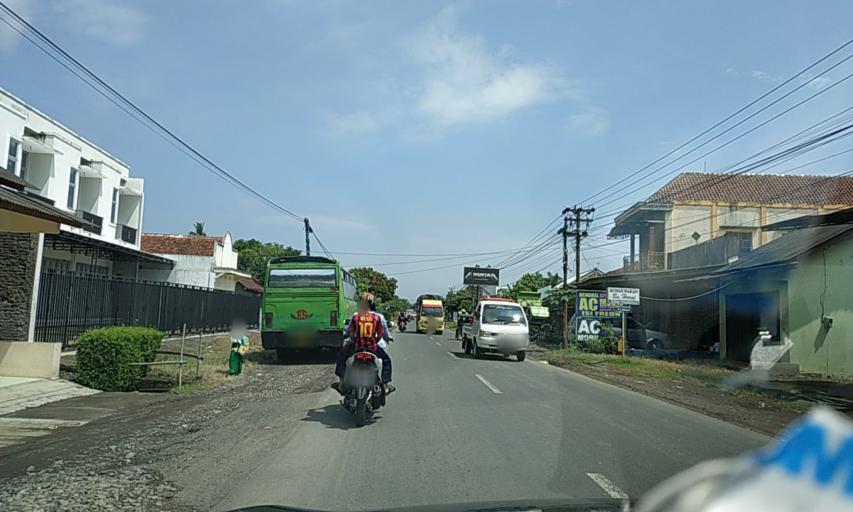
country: ID
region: Central Java
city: Tambangan
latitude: -7.4865
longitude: 108.8185
